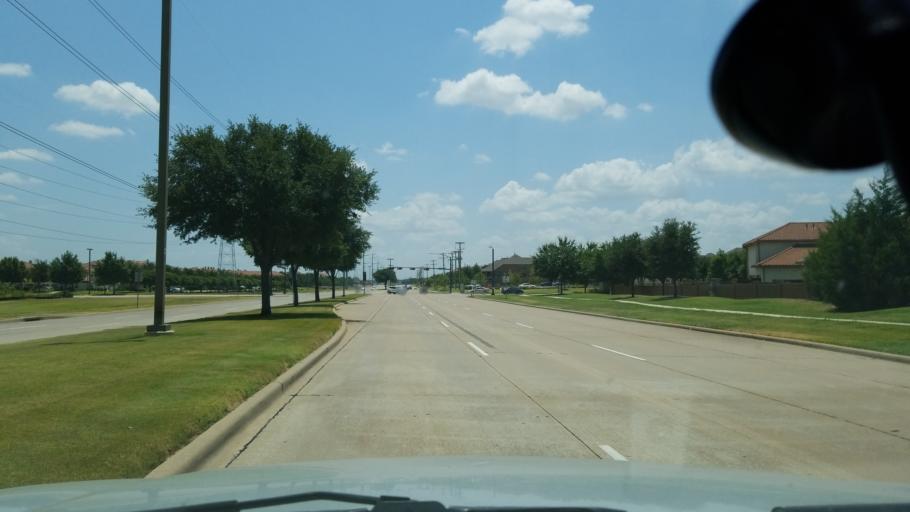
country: US
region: Texas
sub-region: Dallas County
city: Farmers Branch
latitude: 32.9041
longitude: -96.9419
